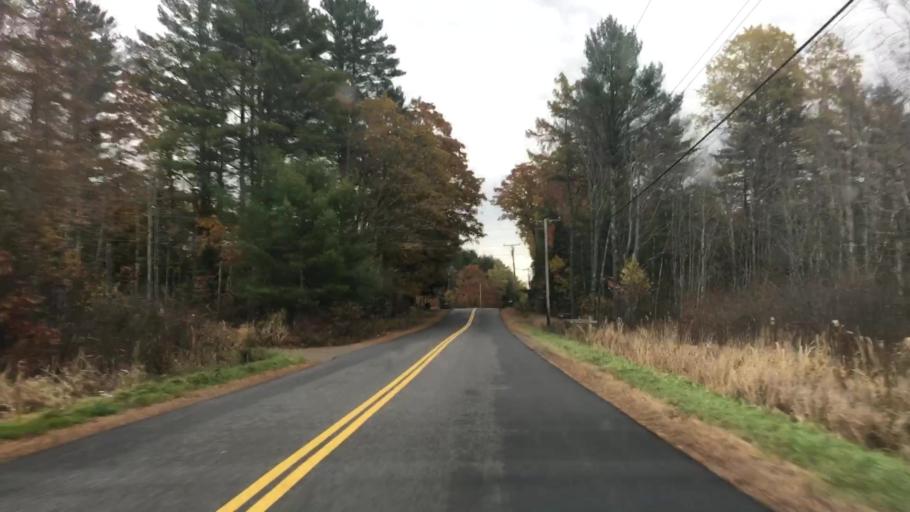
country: US
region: Maine
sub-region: Kennebec County
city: Pittston
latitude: 44.1681
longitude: -69.7072
